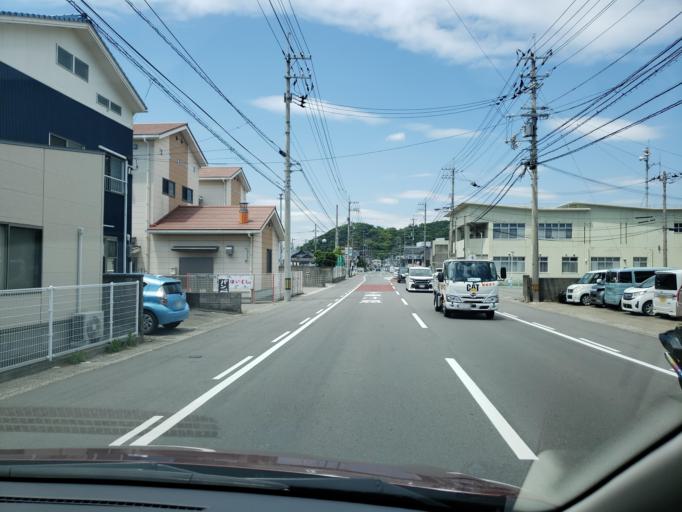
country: JP
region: Tokushima
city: Tokushima-shi
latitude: 34.0443
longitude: 134.5813
